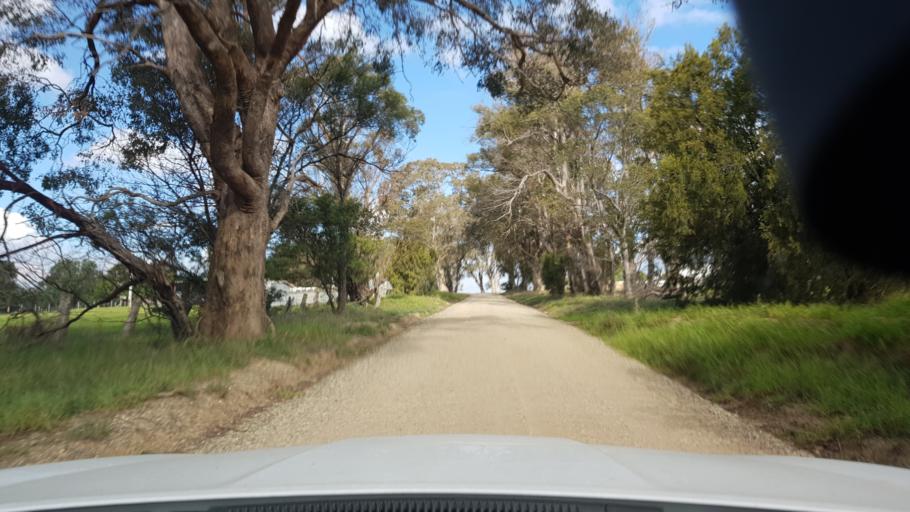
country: AU
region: Victoria
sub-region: East Gippsland
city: Bairnsdale
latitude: -37.7810
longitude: 147.5750
